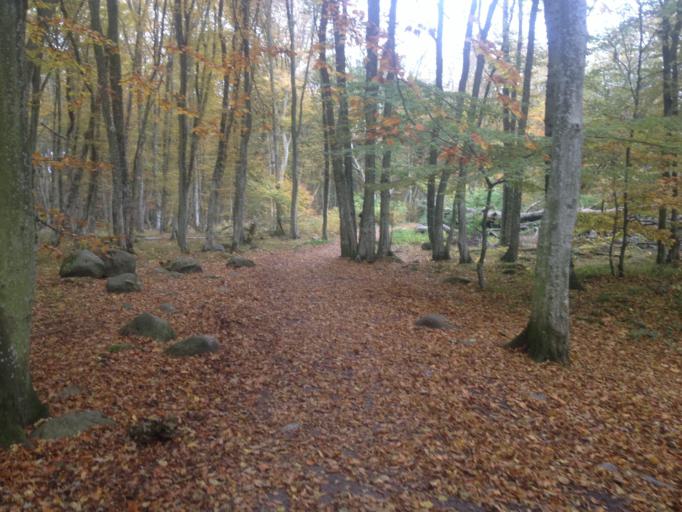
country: SE
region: Skane
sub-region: Simrishamns Kommun
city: Kivik
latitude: 55.6568
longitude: 14.2687
